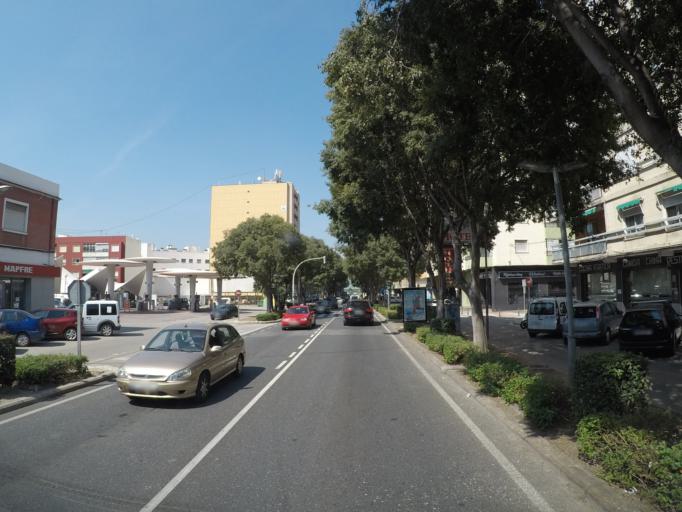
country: ES
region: Valencia
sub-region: Provincia de Valencia
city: Oliva
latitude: 38.9227
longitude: -0.1240
